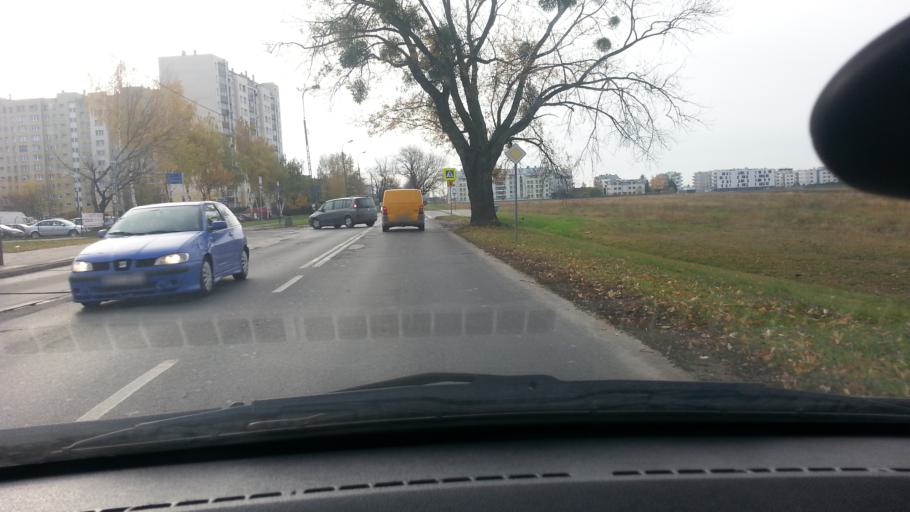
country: PL
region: Masovian Voivodeship
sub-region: Warszawa
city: Bemowo
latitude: 52.2368
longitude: 20.8966
